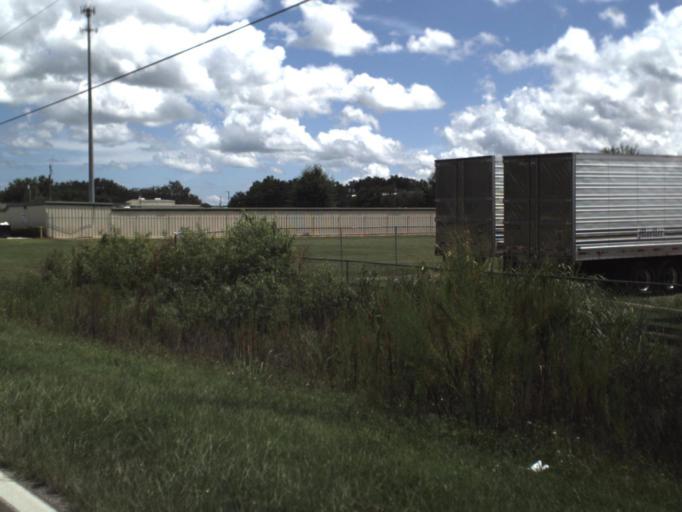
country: US
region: Florida
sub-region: Polk County
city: Lake Hamilton
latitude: 28.0808
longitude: -81.6605
